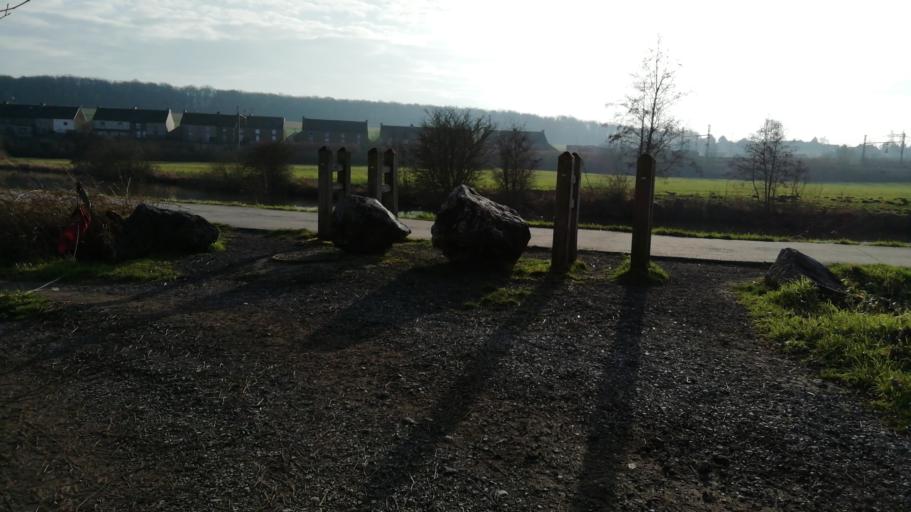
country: FR
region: Nord-Pas-de-Calais
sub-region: Departement du Nord
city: Boussois
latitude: 50.2856
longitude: 4.0528
